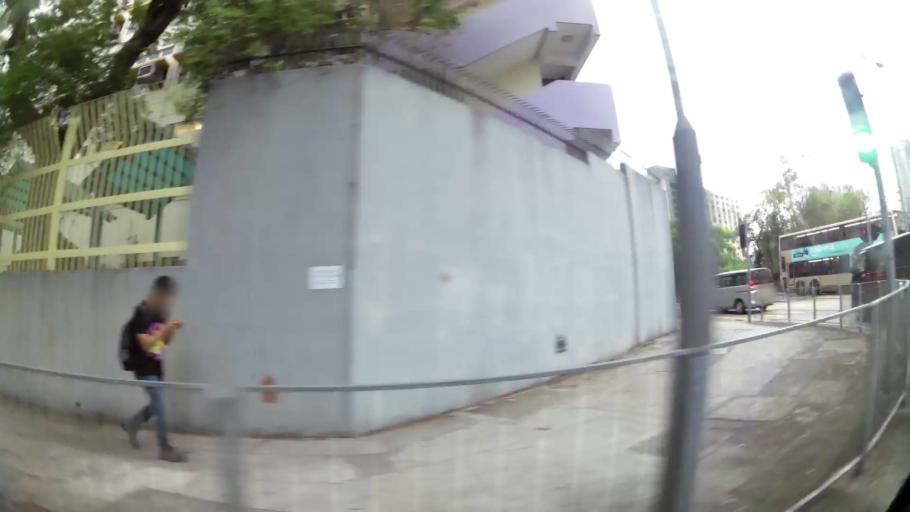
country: HK
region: Tsuen Wan
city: Tsuen Wan
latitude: 22.3589
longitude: 114.1213
